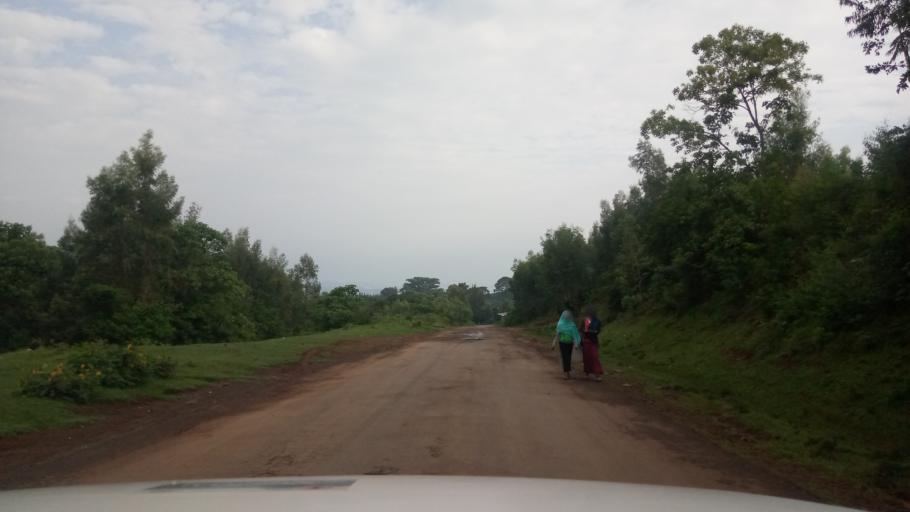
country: ET
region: Oromiya
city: Agaro
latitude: 7.7949
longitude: 36.7229
